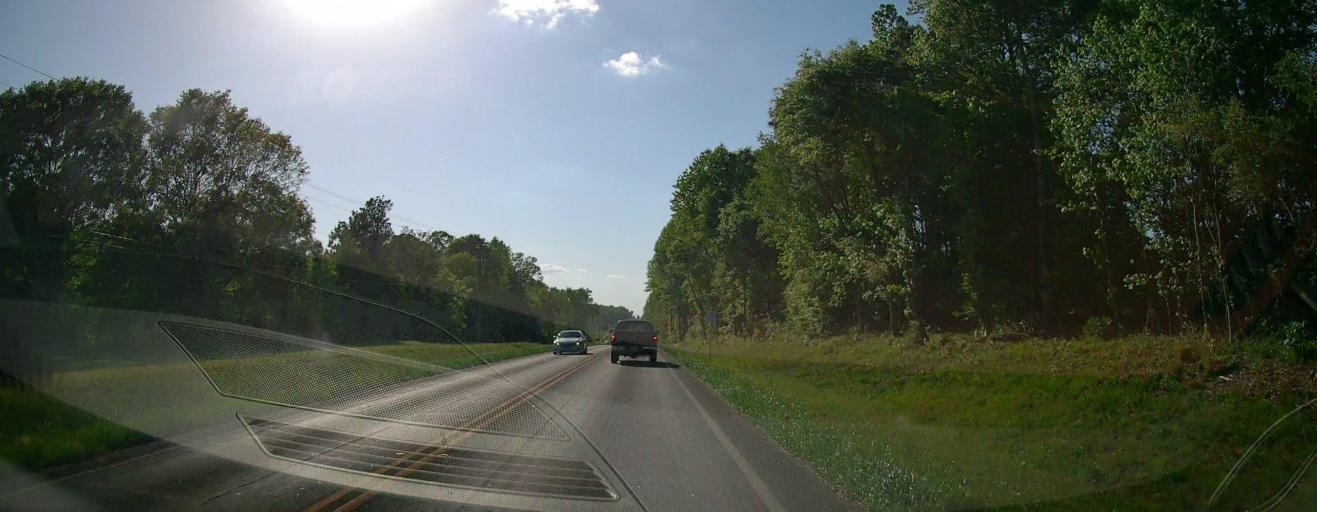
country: US
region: Georgia
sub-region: Morgan County
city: Madison
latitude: 33.5833
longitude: -83.4979
